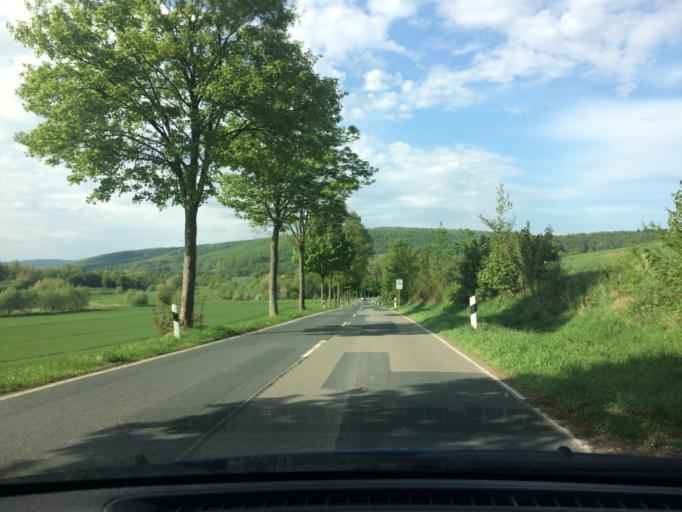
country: DE
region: Lower Saxony
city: Buhren
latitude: 51.5331
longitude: 9.6238
